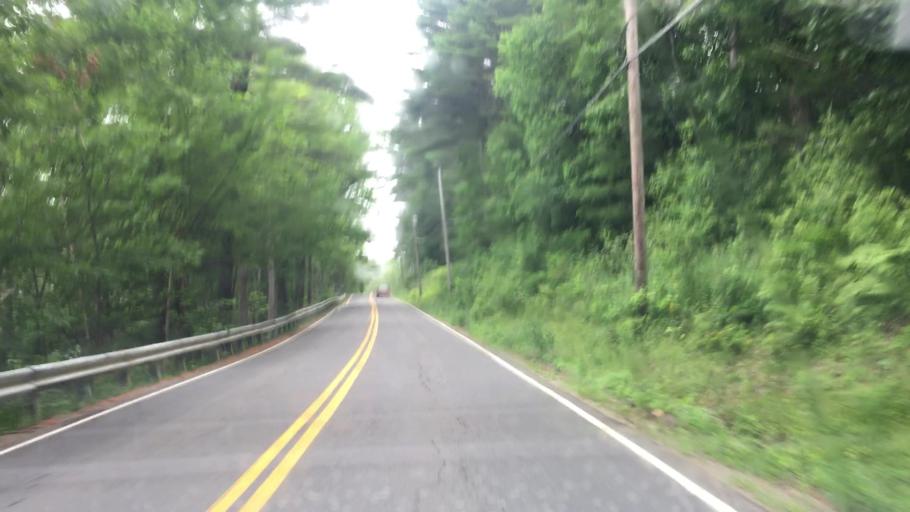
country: US
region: Maine
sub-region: Lincoln County
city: Wiscasset
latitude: 43.9923
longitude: -69.6483
